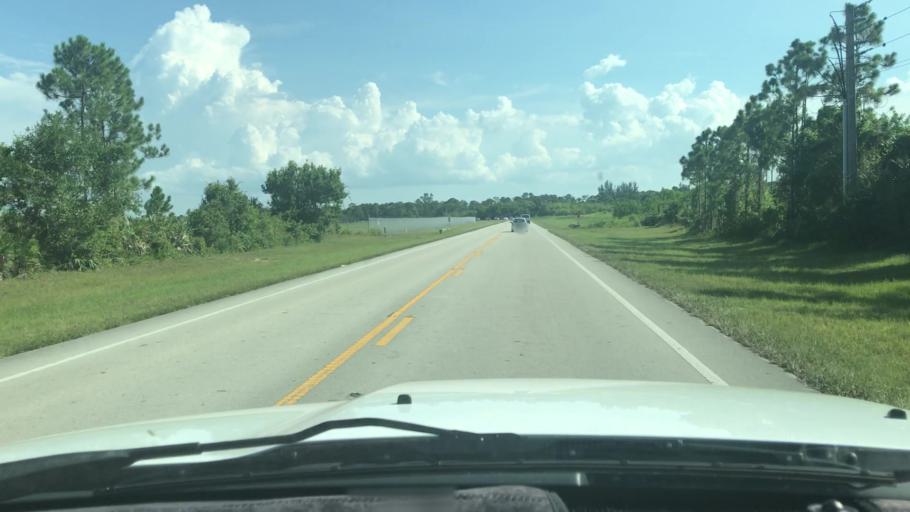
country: US
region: Florida
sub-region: Indian River County
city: Gifford
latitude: 27.6613
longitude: -80.4306
